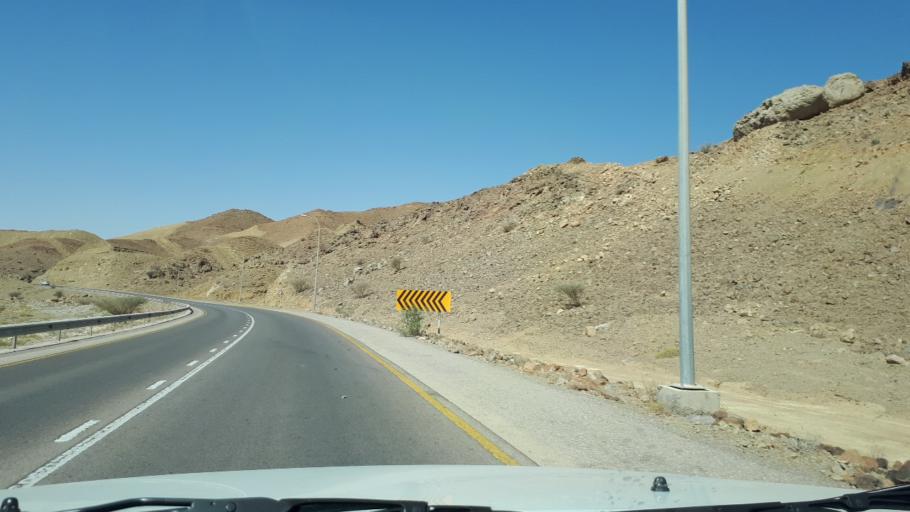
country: OM
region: Ash Sharqiyah
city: Sur
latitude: 22.3374
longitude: 59.3097
